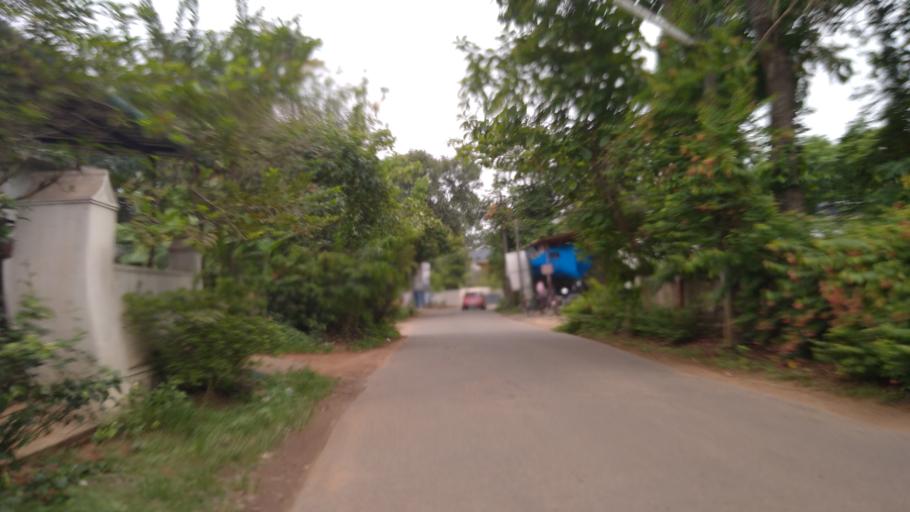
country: IN
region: Kerala
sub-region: Ernakulam
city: Angamali
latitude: 10.1681
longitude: 76.3978
